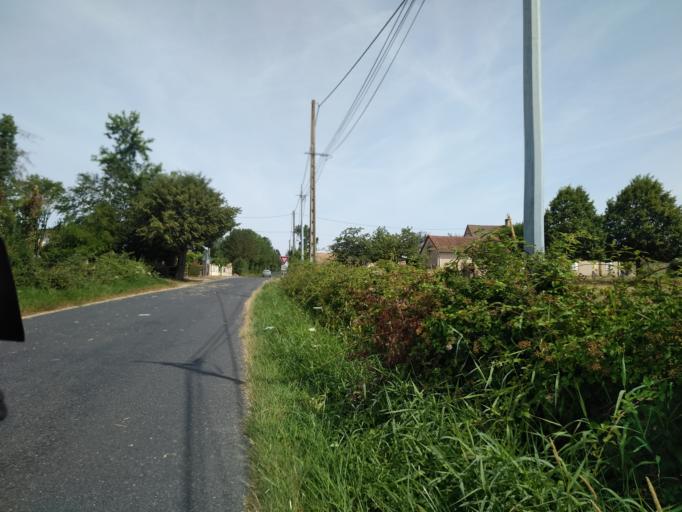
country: FR
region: Auvergne
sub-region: Departement de l'Allier
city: Molinet
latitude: 46.4323
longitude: 3.9741
